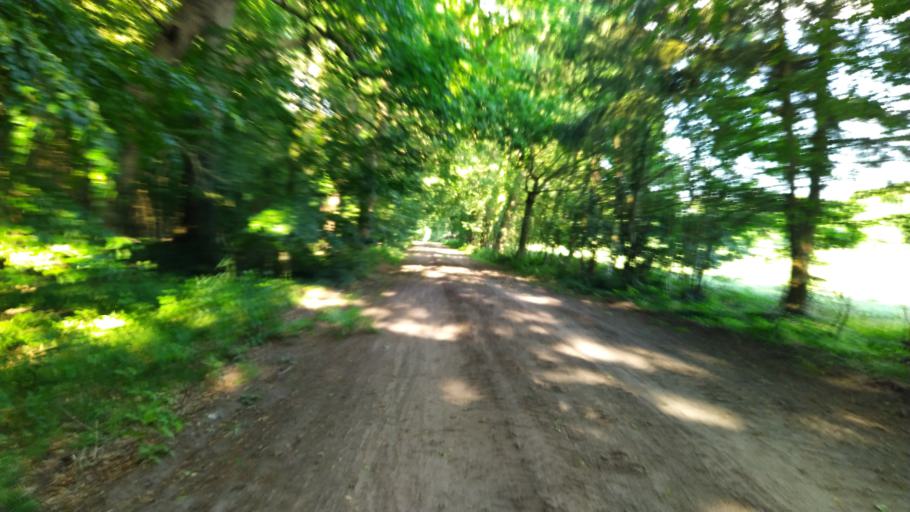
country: DE
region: Lower Saxony
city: Lintig
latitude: 53.5978
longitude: 8.9128
